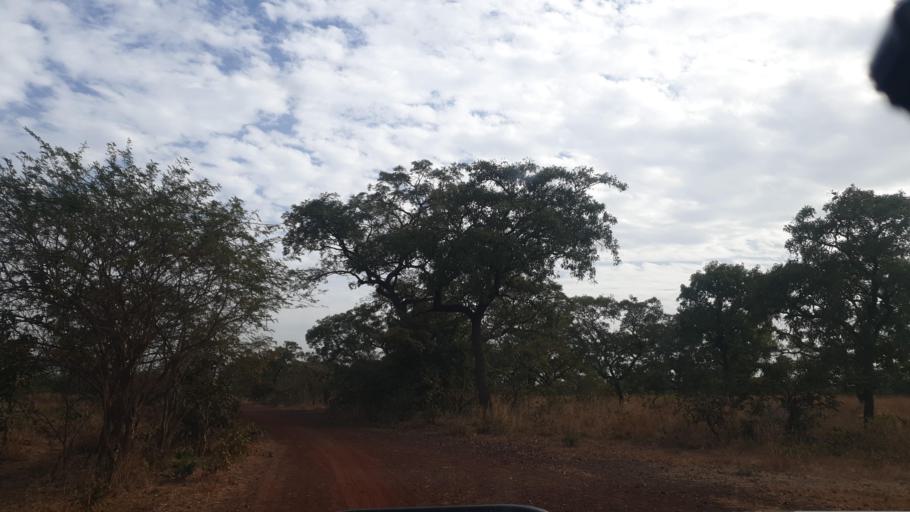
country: ML
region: Sikasso
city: Yanfolila
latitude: 11.4052
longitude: -8.0129
